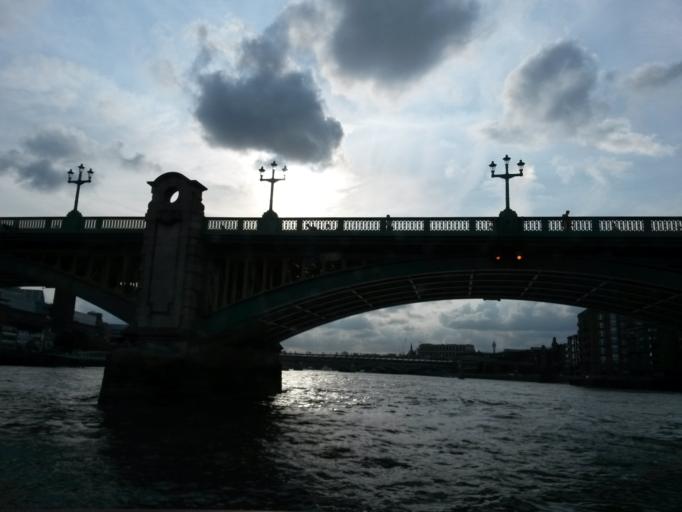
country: GB
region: England
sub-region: Greater London
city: City of London
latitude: 51.5091
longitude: -0.0933
